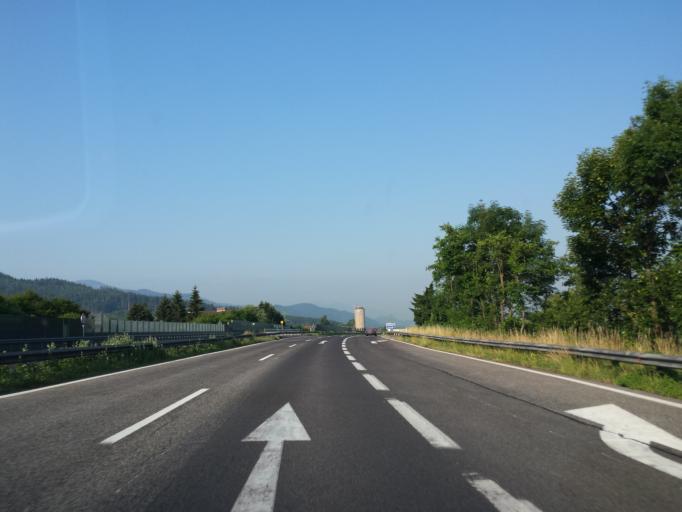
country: AT
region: Styria
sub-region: Politischer Bezirk Bruck-Muerzzuschlag
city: Kindberg
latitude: 47.4979
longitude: 15.4350
